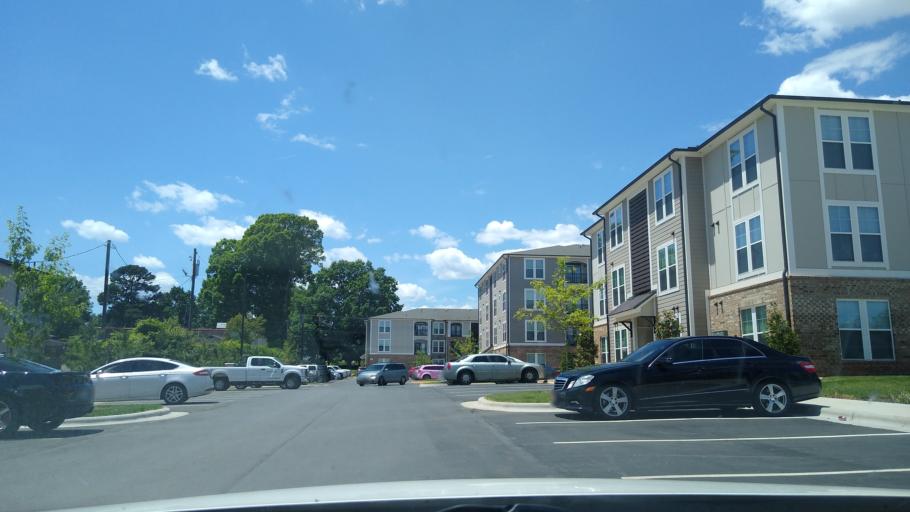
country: US
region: North Carolina
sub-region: Guilford County
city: Jamestown
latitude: 36.0665
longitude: -79.9078
